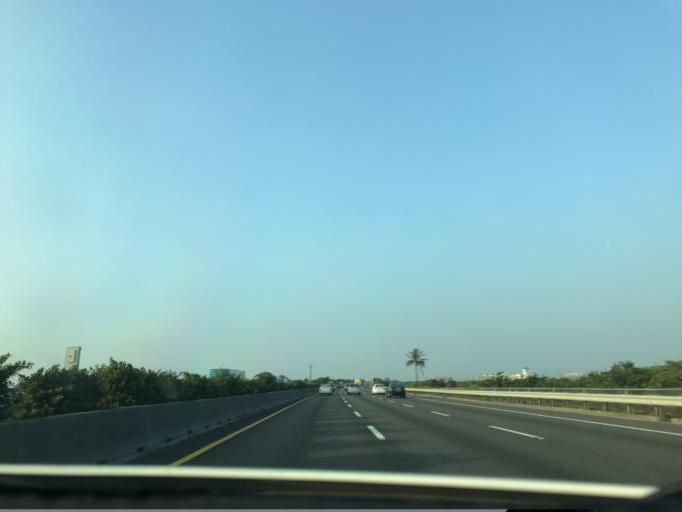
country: TW
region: Taiwan
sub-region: Tainan
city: Tainan
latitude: 23.1491
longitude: 120.2312
